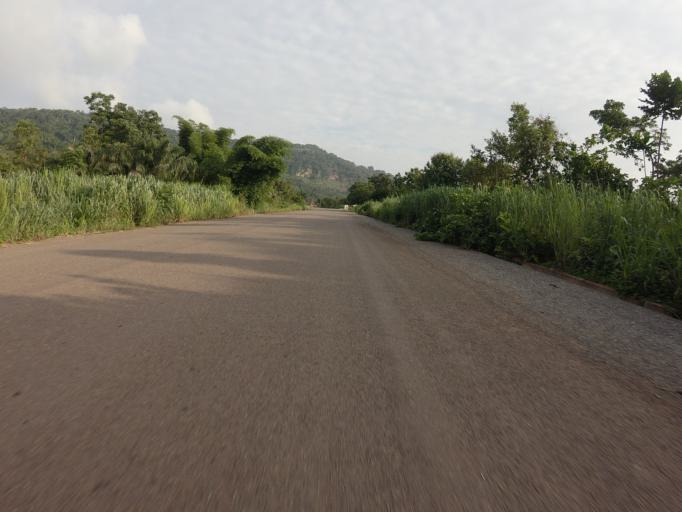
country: TG
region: Plateaux
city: Kpalime
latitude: 6.9241
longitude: 0.4614
